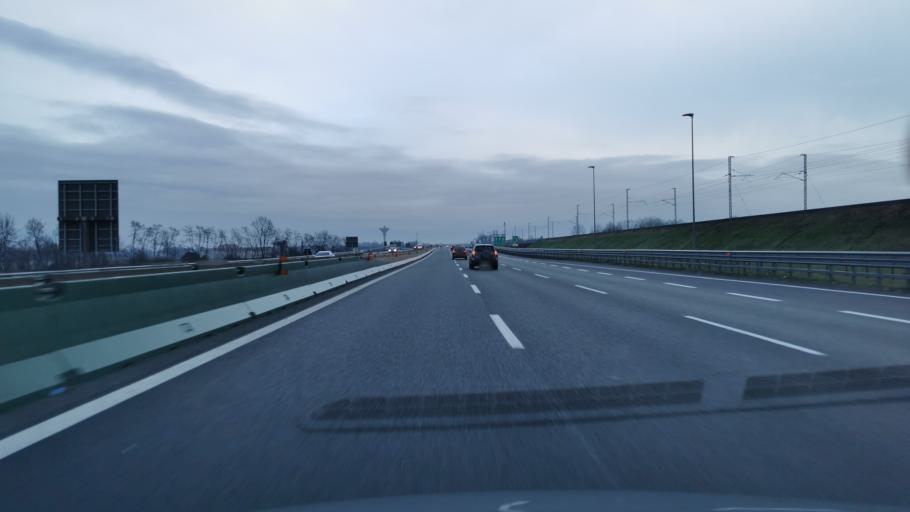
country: IT
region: Piedmont
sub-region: Provincia di Torino
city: Brandizzo
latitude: 45.1755
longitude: 7.8174
